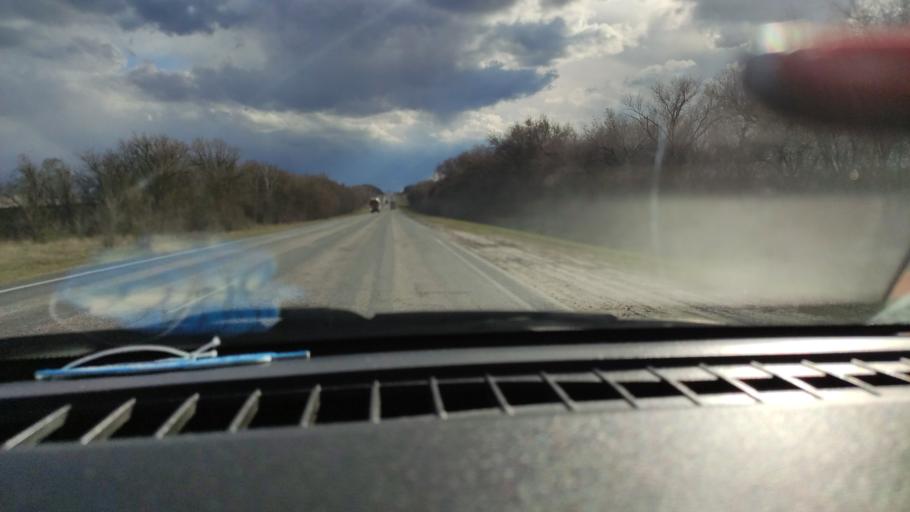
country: RU
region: Saratov
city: Sinodskoye
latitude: 51.9651
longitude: 46.6314
